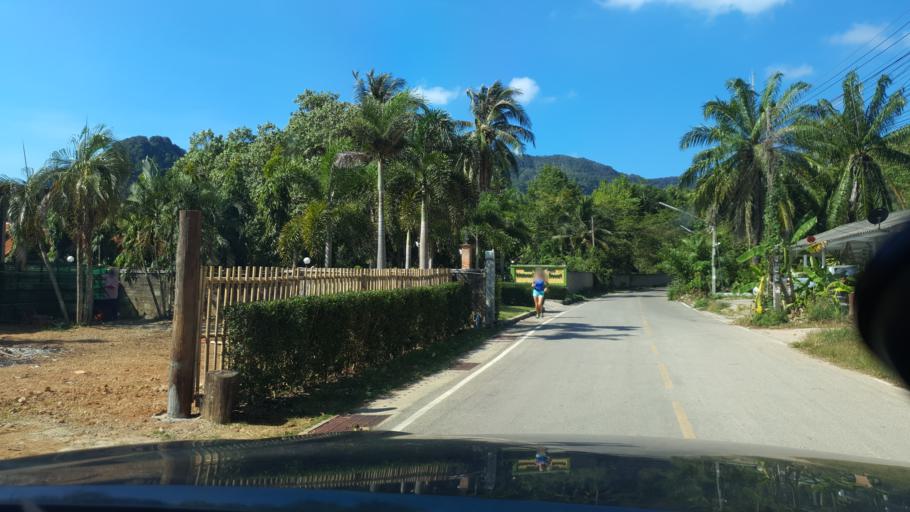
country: TH
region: Phangnga
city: Ban Ao Nang
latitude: 8.0298
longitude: 98.8608
